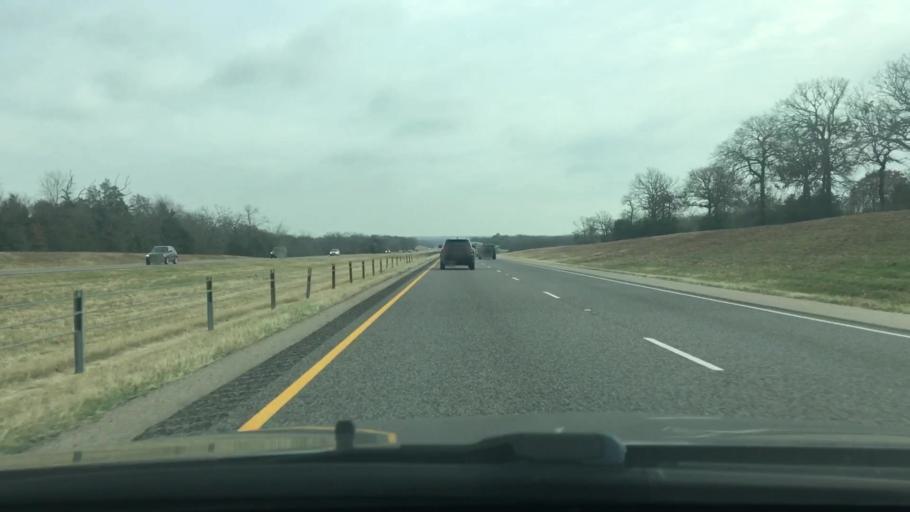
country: US
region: Texas
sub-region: Leon County
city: Buffalo
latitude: 31.5283
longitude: -96.1151
